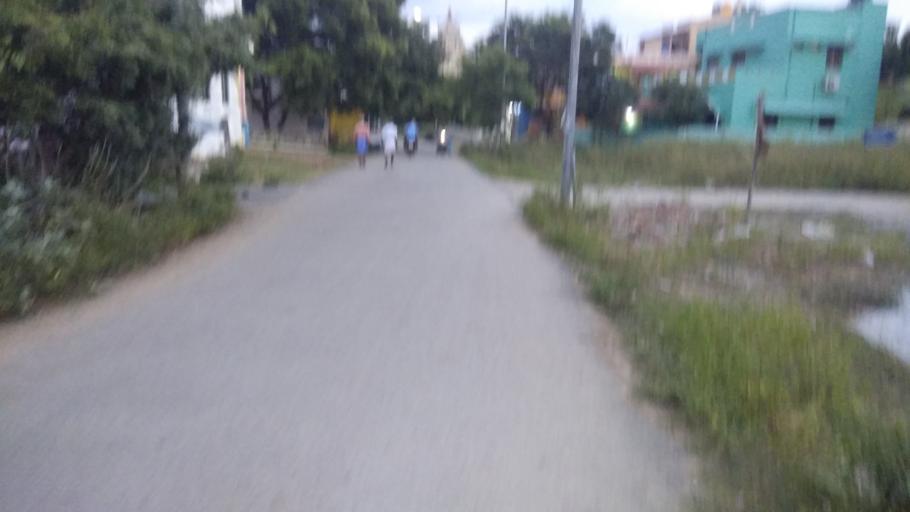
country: IN
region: Tamil Nadu
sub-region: Thiruvallur
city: Tiruvallur
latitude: 13.1216
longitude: 79.9207
